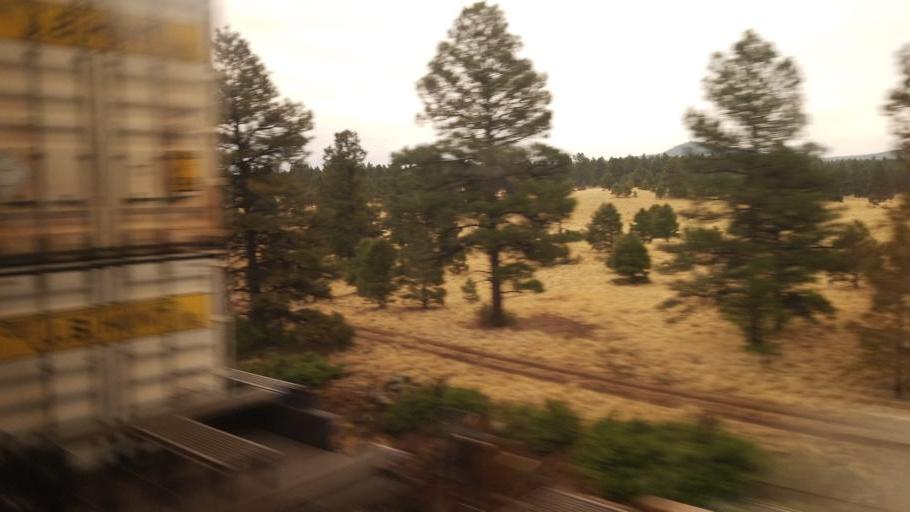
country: US
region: Arizona
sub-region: Coconino County
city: Parks
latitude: 35.2468
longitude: -111.9694
